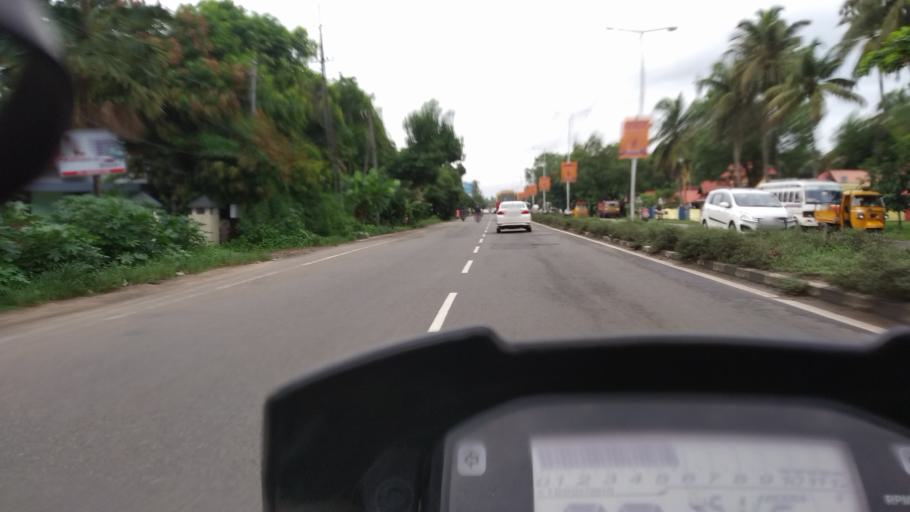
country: IN
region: Kerala
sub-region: Alappuzha
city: Kutiatodu
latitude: 9.8325
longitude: 76.3094
